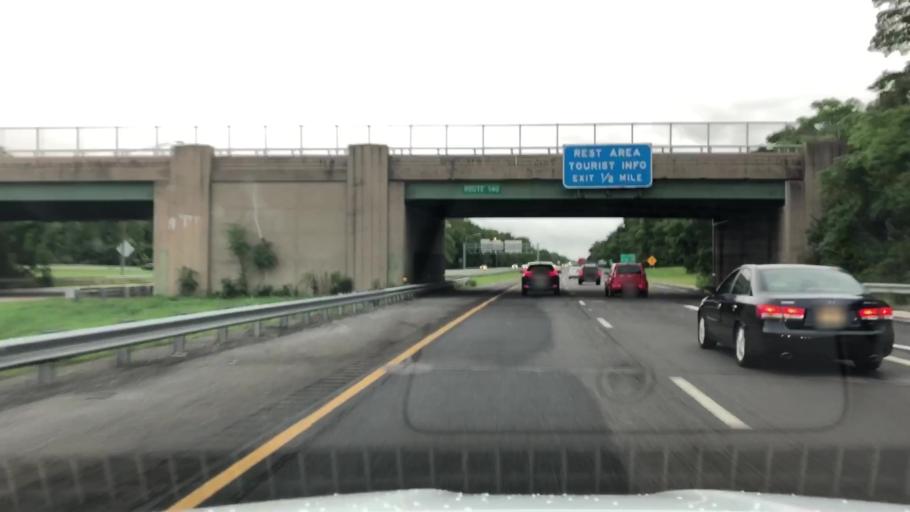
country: US
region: New Jersey
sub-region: Salem County
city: Carneys Point
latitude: 39.6829
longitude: -75.4810
